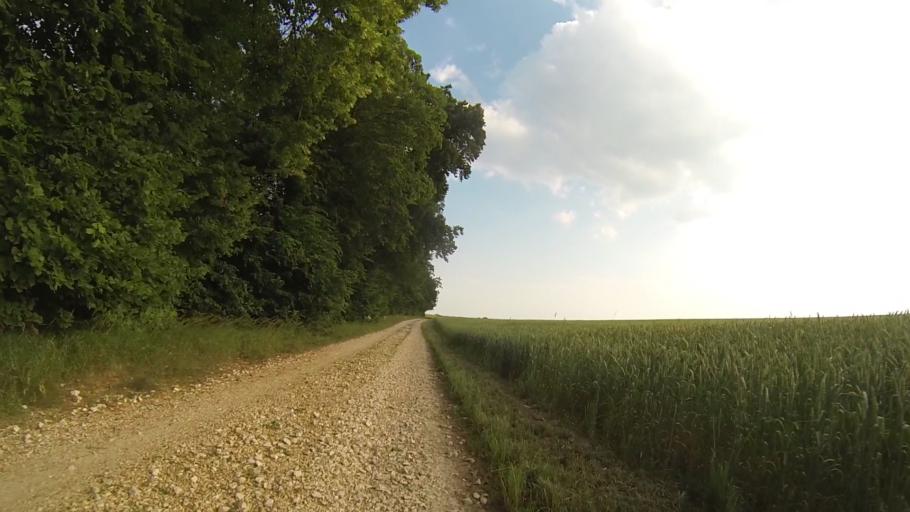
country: DE
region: Baden-Wuerttemberg
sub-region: Tuebingen Region
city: Blaubeuren
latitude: 48.4418
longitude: 9.8615
